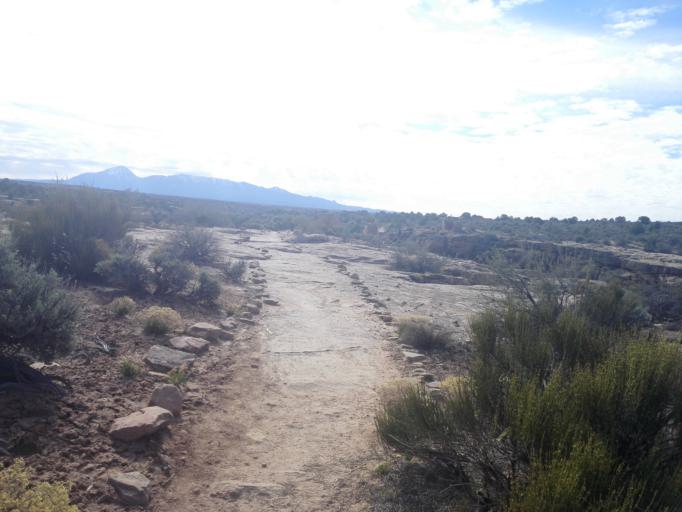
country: US
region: Colorado
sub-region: Montezuma County
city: Towaoc
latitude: 37.3846
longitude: -109.0786
